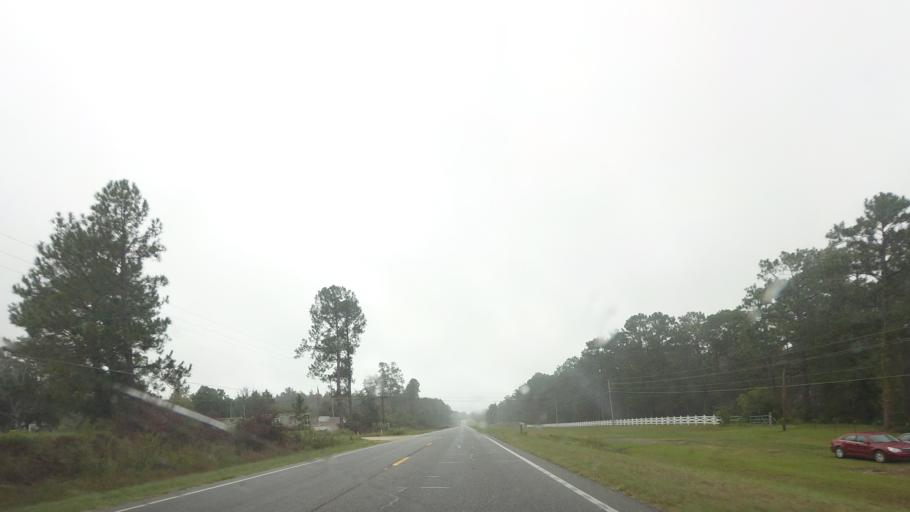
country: US
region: Georgia
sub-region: Ben Hill County
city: Fitzgerald
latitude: 31.7557
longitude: -83.2458
